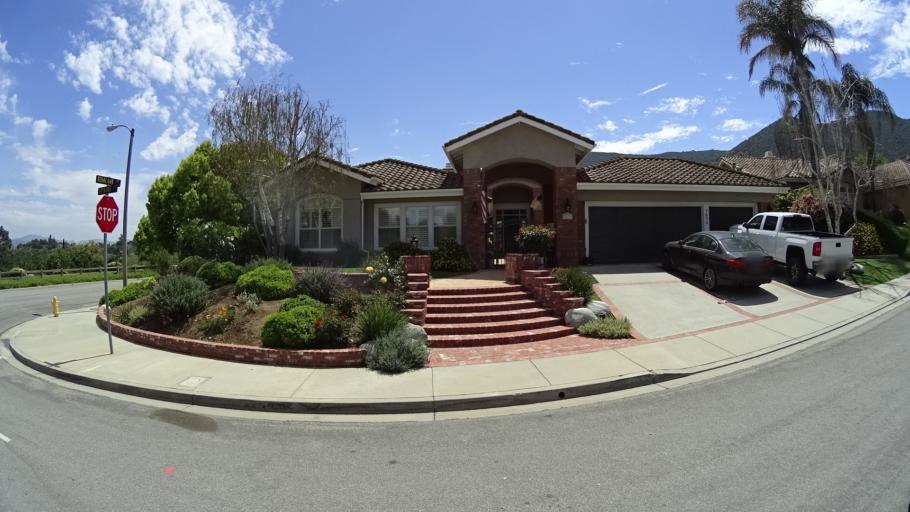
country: US
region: California
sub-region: Ventura County
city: Casa Conejo
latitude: 34.1742
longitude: -118.9153
